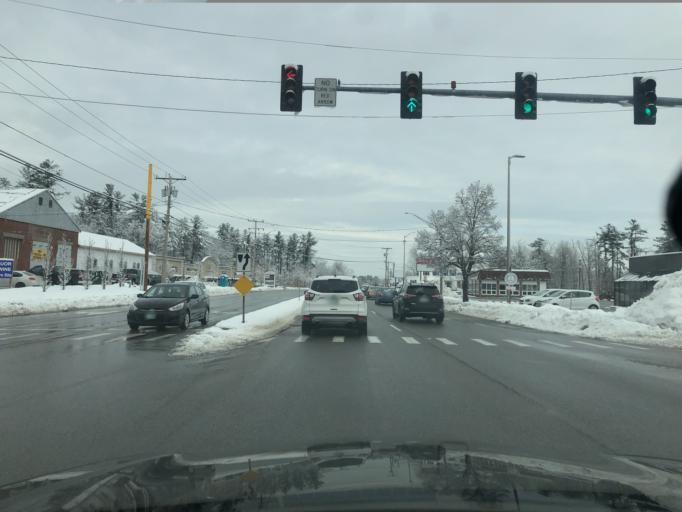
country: US
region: New Hampshire
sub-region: Strafford County
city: Dover
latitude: 43.2273
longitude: -70.8834
